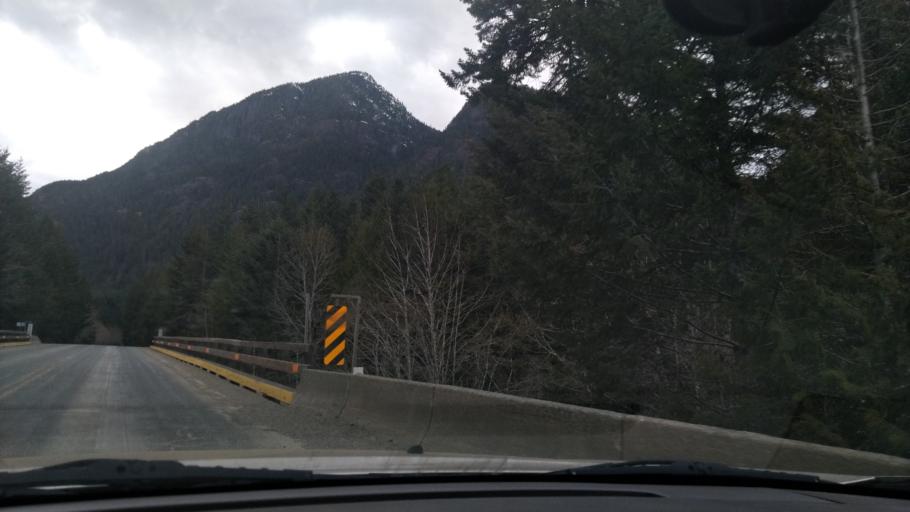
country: CA
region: British Columbia
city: Campbell River
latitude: 49.8538
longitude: -125.8260
